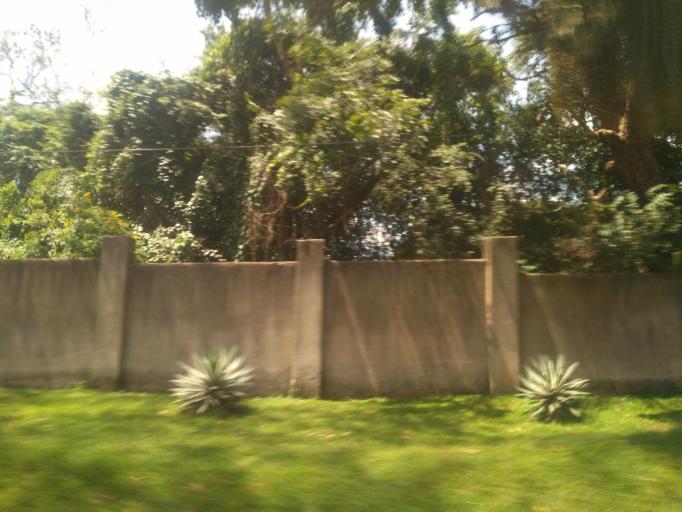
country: UG
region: Central Region
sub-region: Wakiso District
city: Entebbe
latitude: 0.0479
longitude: 32.4636
